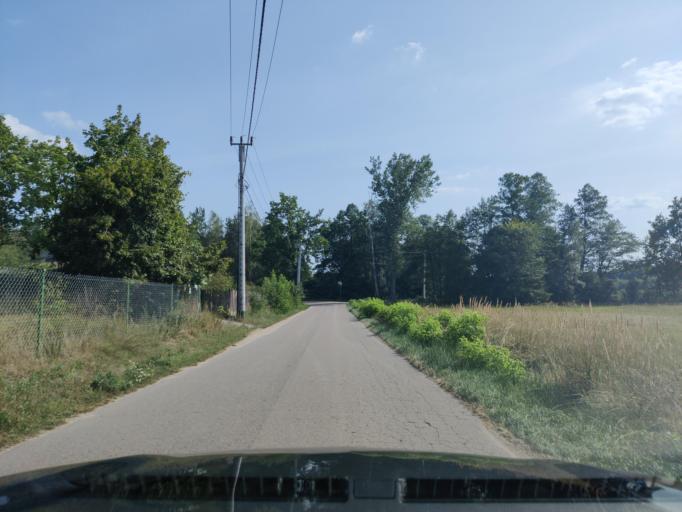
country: PL
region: Masovian Voivodeship
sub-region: Powiat makowski
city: Rozan
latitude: 52.8482
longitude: 21.4576
